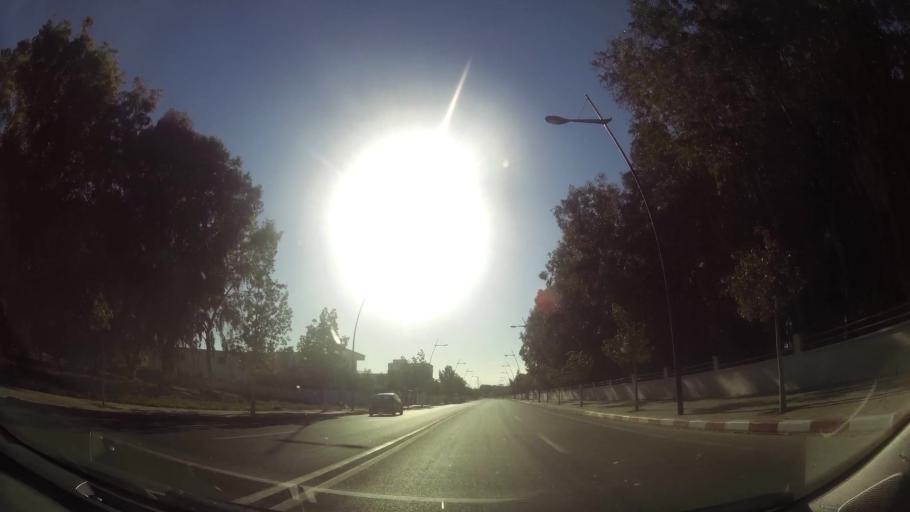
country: MA
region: Oriental
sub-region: Berkane-Taourirt
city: Madagh
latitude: 35.0875
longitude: -2.2360
